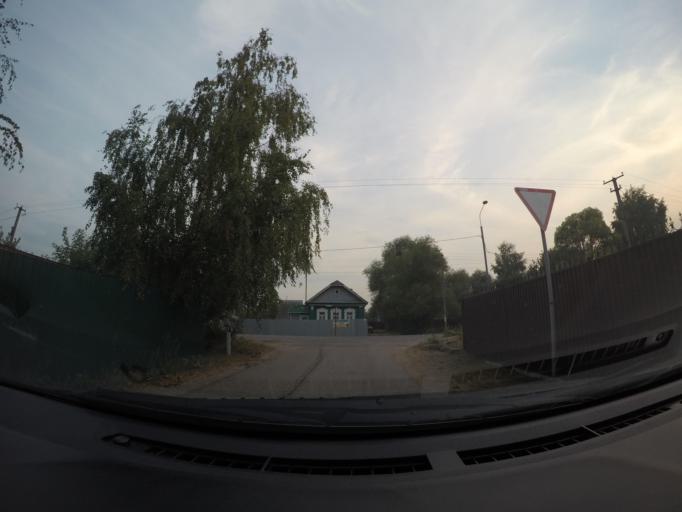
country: RU
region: Moskovskaya
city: Imeni Tsyurupy
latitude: 55.4956
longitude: 38.6581
